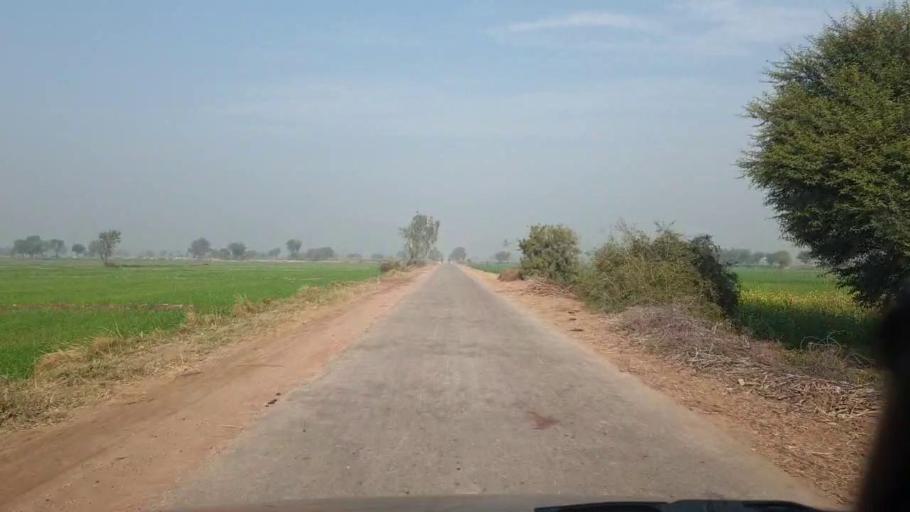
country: PK
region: Sindh
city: Shahdadpur
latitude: 25.9654
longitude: 68.5828
